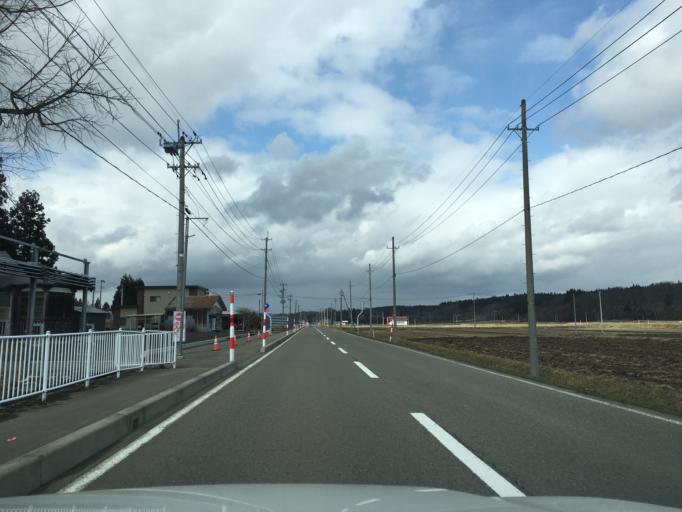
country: JP
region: Akita
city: Takanosu
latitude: 40.1343
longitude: 140.3557
